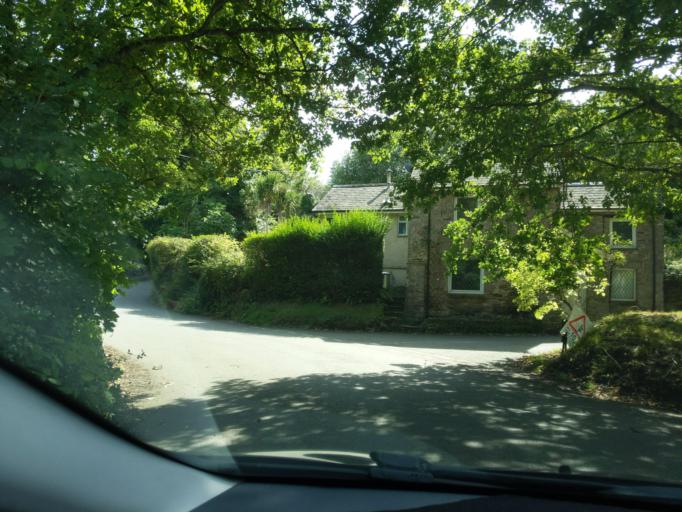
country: GB
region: England
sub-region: Cornwall
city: Torpoint
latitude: 50.3619
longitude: -4.2403
